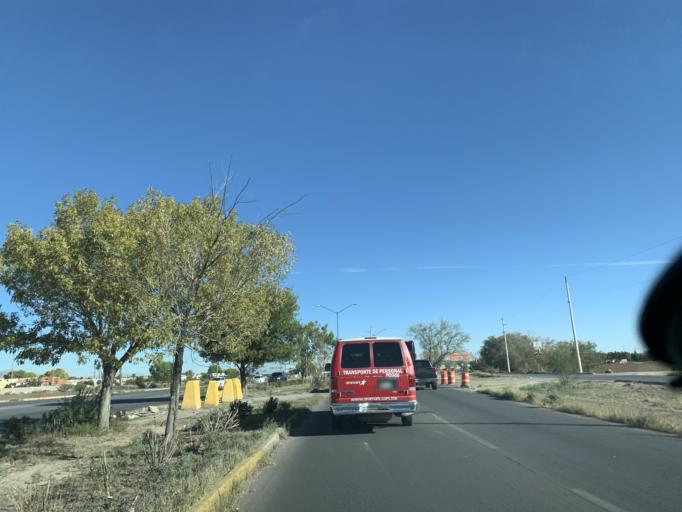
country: US
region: Texas
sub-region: El Paso County
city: Socorro
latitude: 31.7036
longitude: -106.3826
